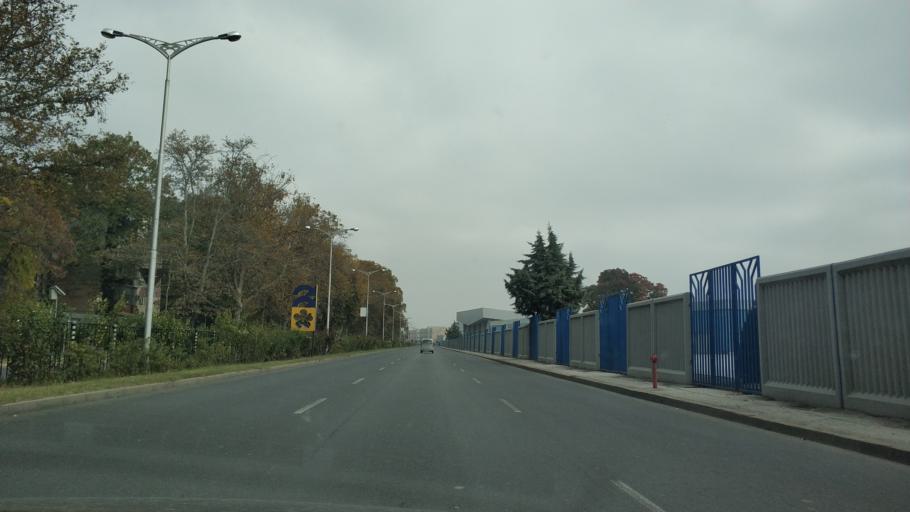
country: BG
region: Plovdiv
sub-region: Obshtina Plovdiv
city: Plovdiv
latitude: 42.1592
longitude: 24.7509
